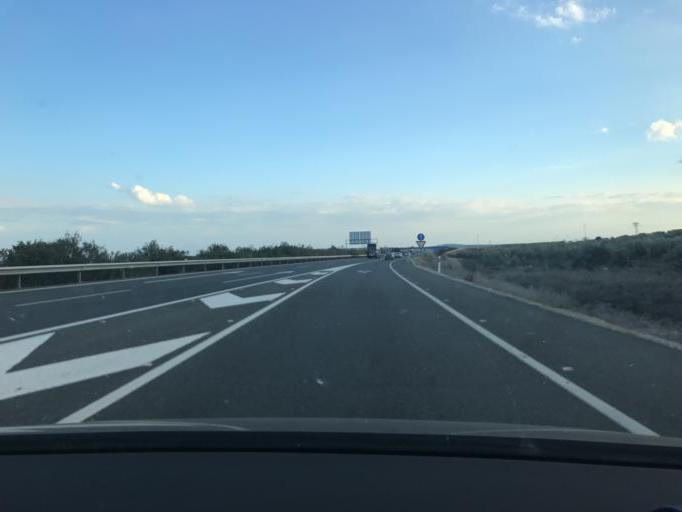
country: ES
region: Andalusia
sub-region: Provincia de Jaen
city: Bailen
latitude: 38.0961
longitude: -3.7399
